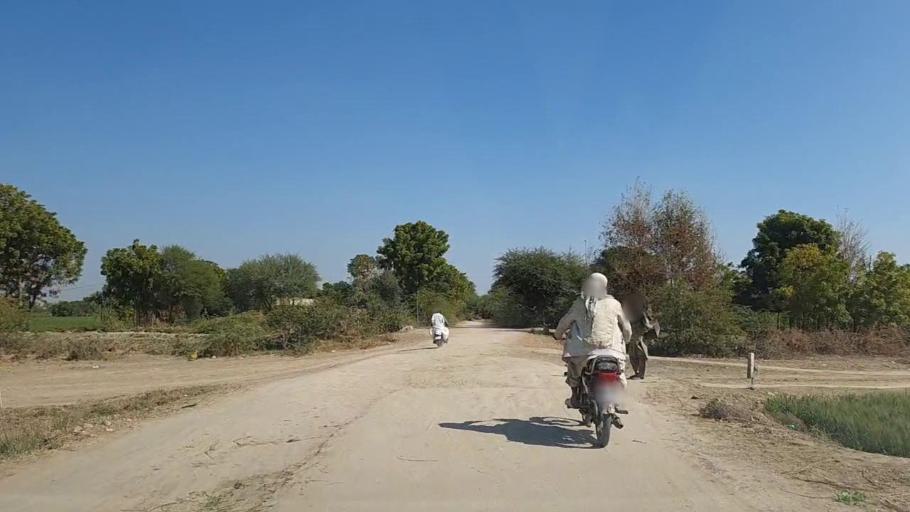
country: PK
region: Sindh
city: Nawabshah
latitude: 26.2386
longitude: 68.4472
